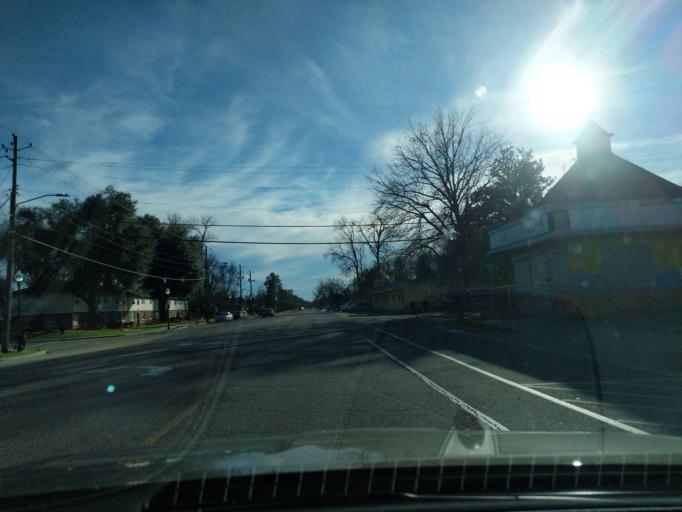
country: US
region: Georgia
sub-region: Richmond County
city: Augusta
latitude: 33.4665
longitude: -81.9494
